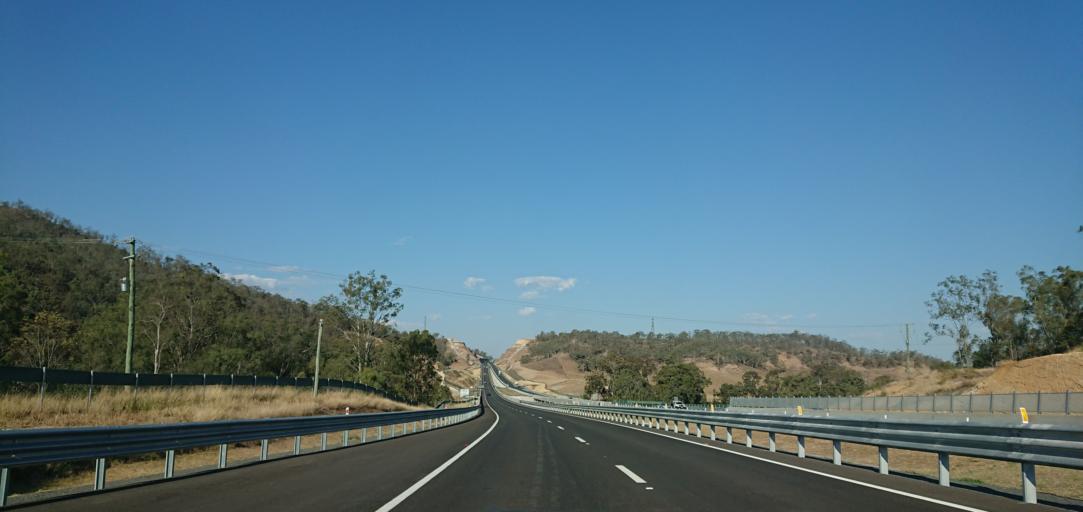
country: AU
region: Queensland
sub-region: Toowoomba
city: East Toowoomba
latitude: -27.5154
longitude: 152.0258
